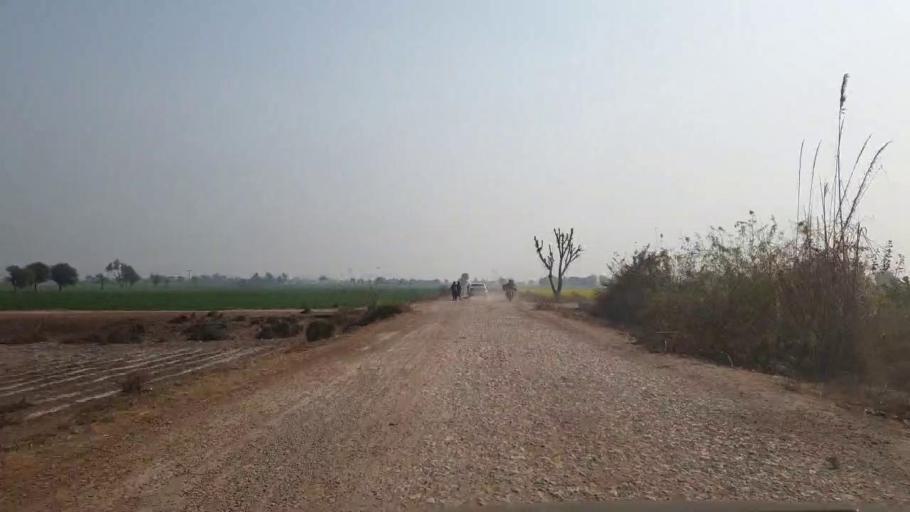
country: PK
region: Sindh
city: Hala
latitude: 25.9450
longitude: 68.4333
